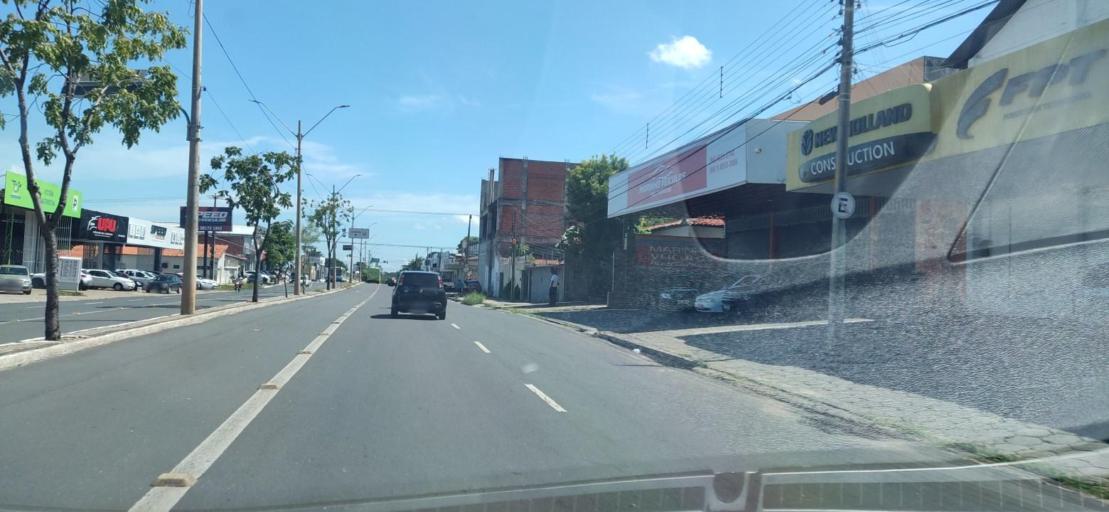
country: BR
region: Piaui
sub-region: Teresina
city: Teresina
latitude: -5.1079
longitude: -42.8082
